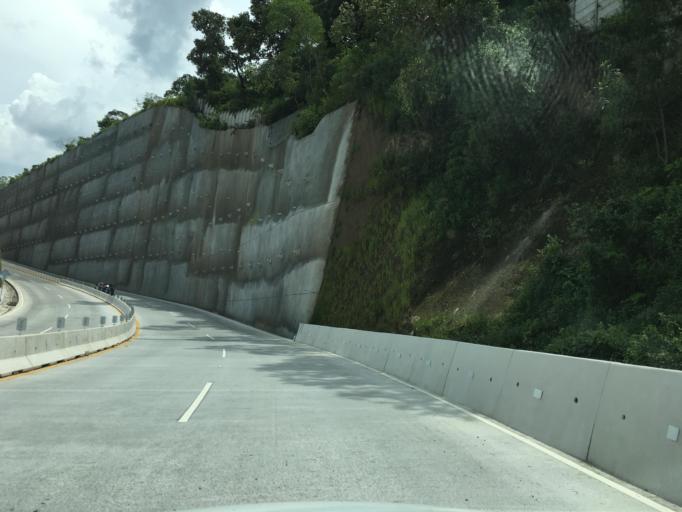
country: GT
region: Guatemala
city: Petapa
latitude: 14.5359
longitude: -90.5355
